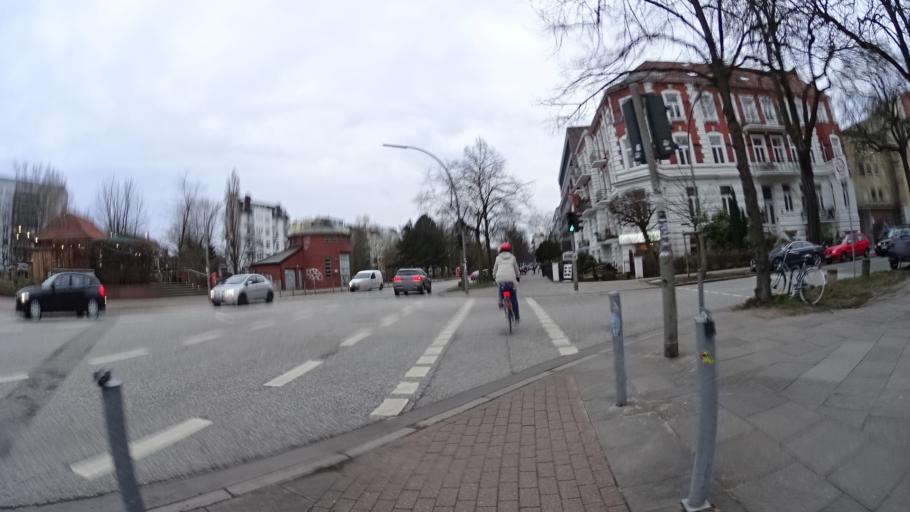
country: DE
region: Hamburg
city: Hamburg-Nord
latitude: 53.5815
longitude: 9.9794
